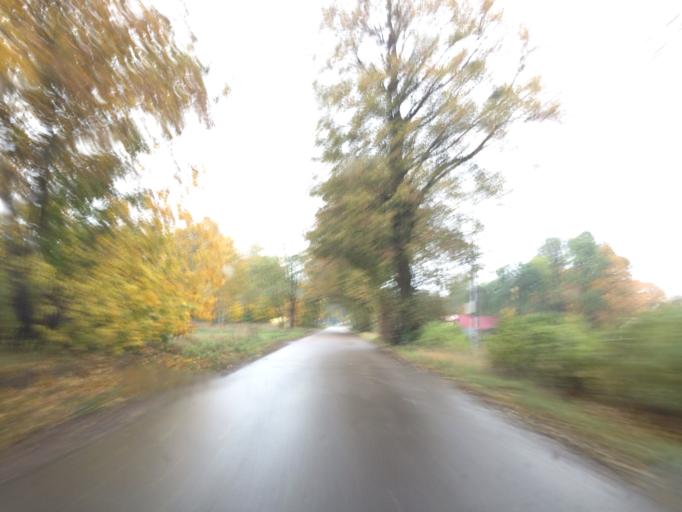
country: PL
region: Warmian-Masurian Voivodeship
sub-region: Powiat nowomiejski
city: Biskupiec
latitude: 53.5826
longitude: 19.4245
